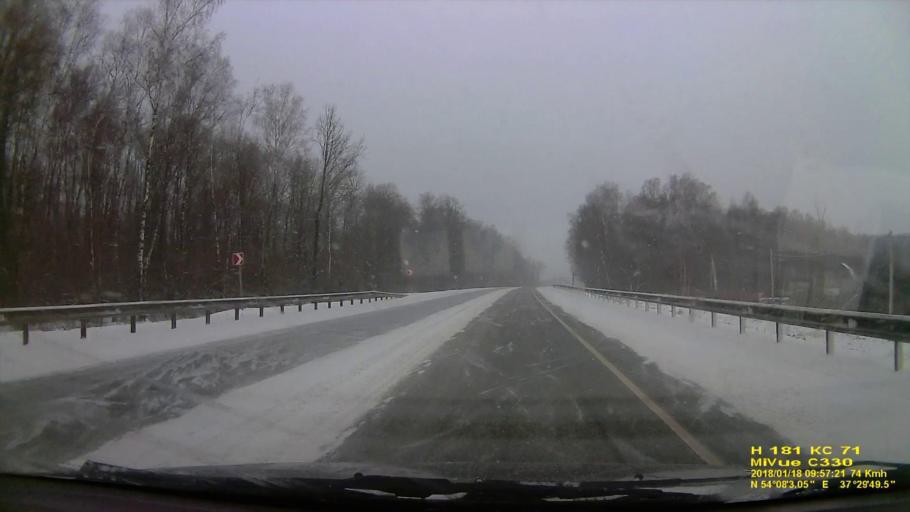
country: RU
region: Tula
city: Kosaya Gora
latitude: 54.1341
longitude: 37.4973
